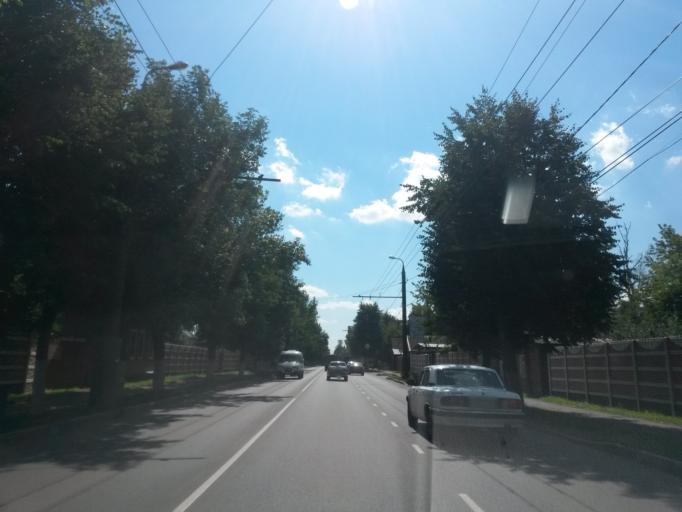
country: RU
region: Ivanovo
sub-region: Gorod Ivanovo
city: Ivanovo
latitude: 56.9901
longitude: 40.9847
